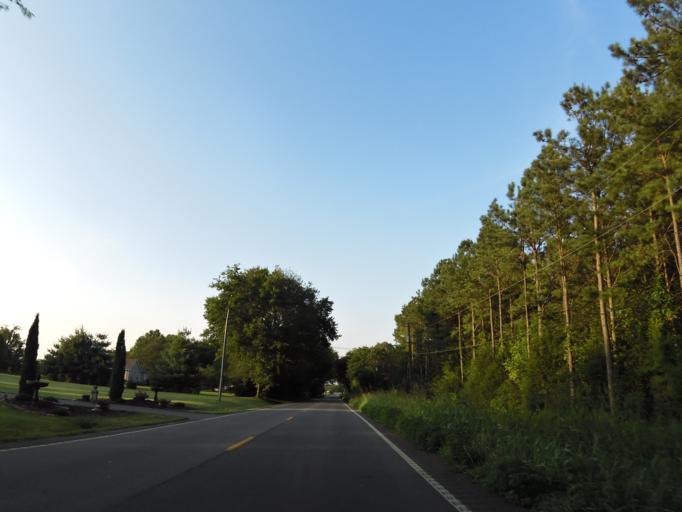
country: US
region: Tennessee
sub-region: Monroe County
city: Sweetwater
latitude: 35.5398
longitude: -84.5216
